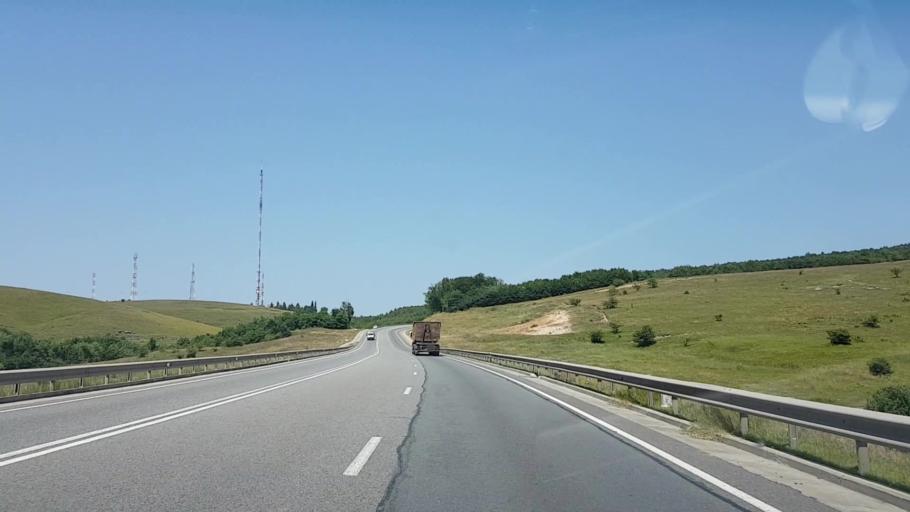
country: RO
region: Cluj
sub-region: Comuna Feleacu
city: Feleacu
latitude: 46.7026
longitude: 23.6414
